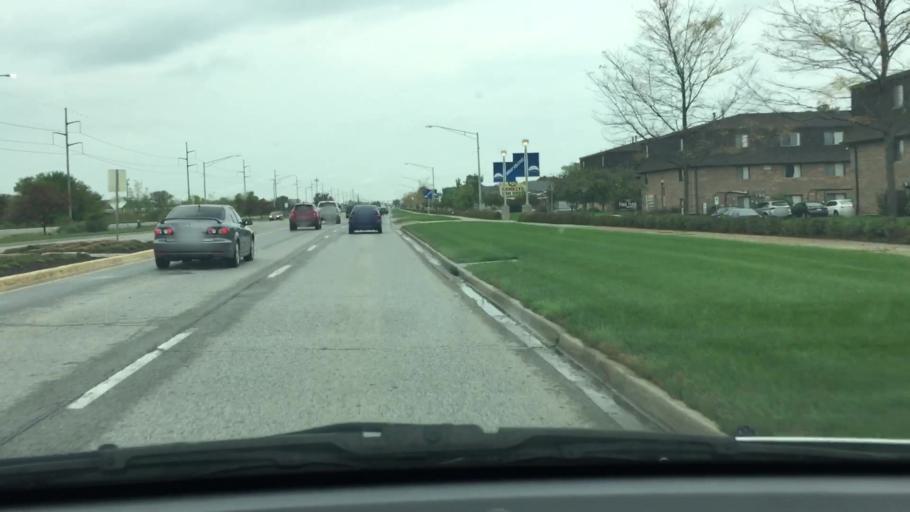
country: US
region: Iowa
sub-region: Johnson County
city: Coralville
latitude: 41.6756
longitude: -91.5838
